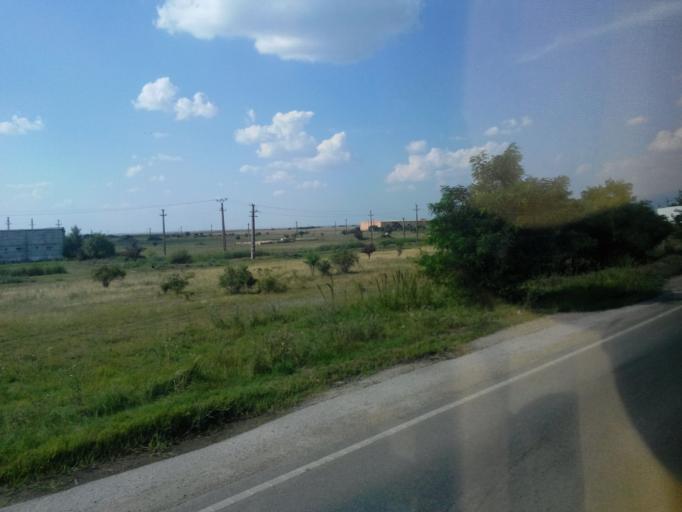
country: RO
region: Timis
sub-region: Comuna Dumbravita
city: Dumbravita
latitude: 45.8157
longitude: 21.2653
